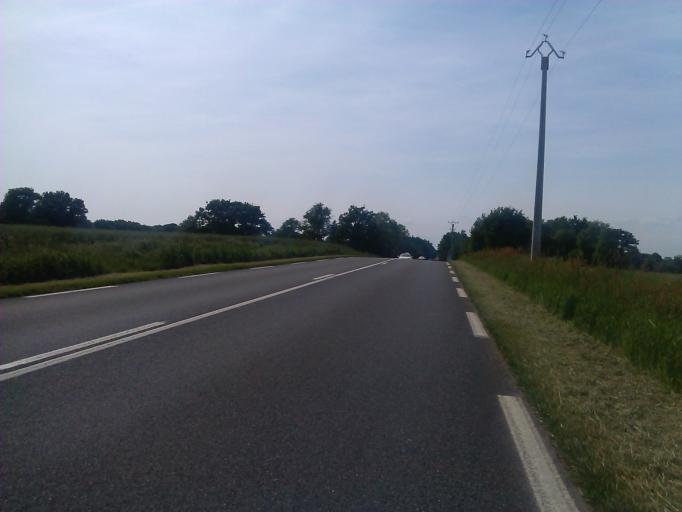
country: FR
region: Centre
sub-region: Departement de l'Indre
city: La Chatre
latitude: 46.5558
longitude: 2.0765
